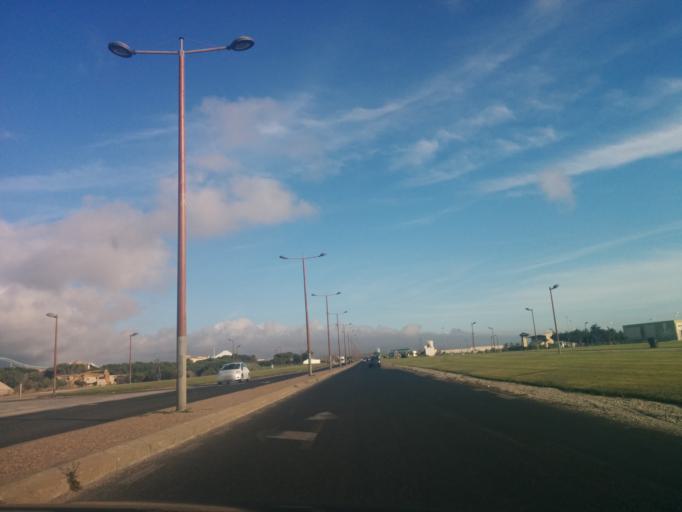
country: PT
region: Leiria
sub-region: Peniche
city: Peniche
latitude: 39.3571
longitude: -9.3646
